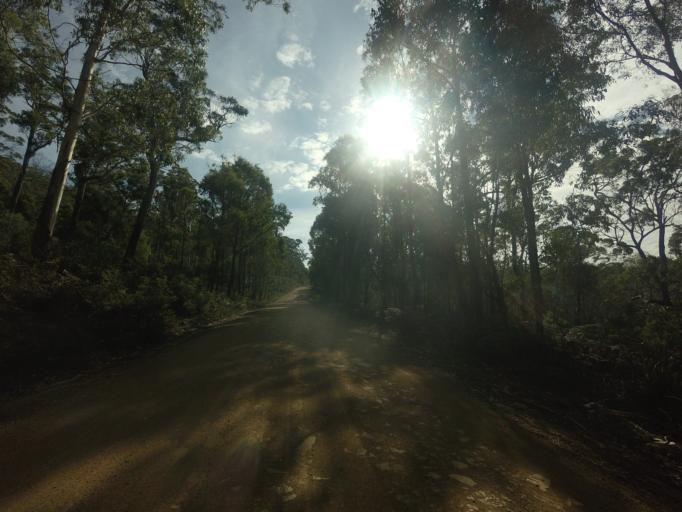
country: AU
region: Tasmania
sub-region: Sorell
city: Sorell
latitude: -42.5576
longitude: 147.4597
